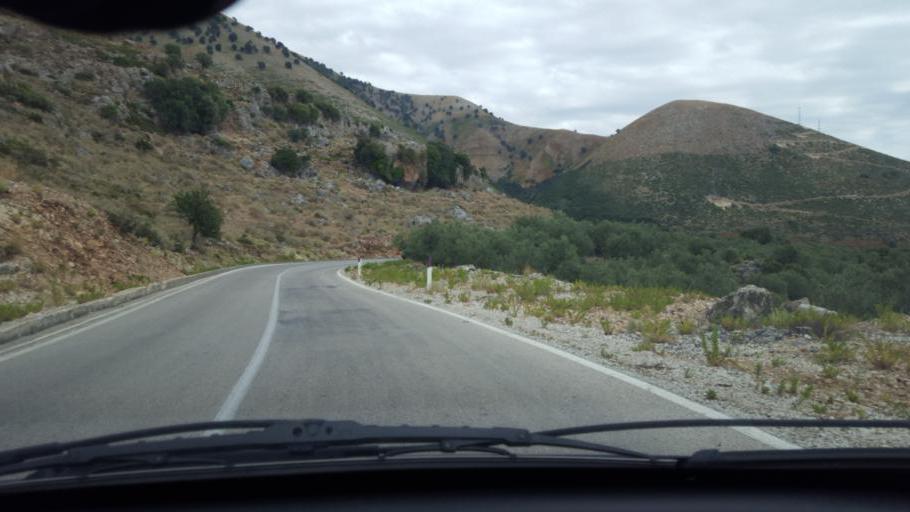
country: AL
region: Vlore
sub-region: Rrethi i Sarandes
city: Lukove
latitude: 40.0364
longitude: 19.8814
